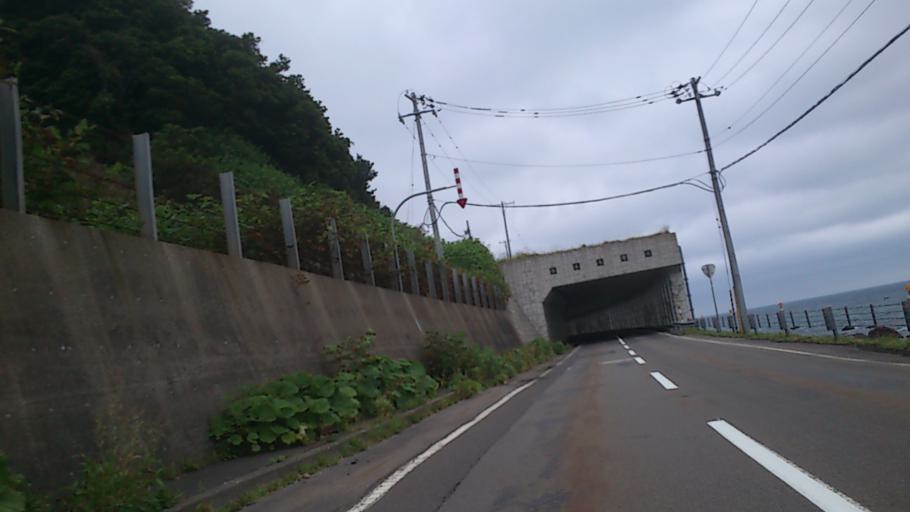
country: JP
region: Hokkaido
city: Iwanai
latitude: 42.6875
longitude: 139.9339
